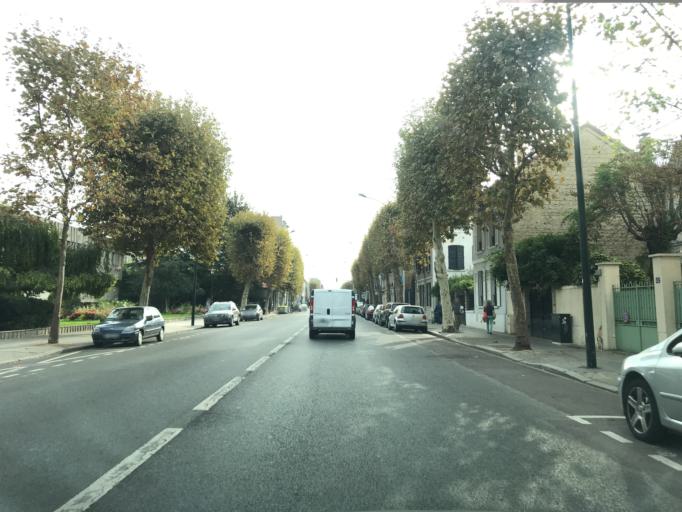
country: FR
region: Ile-de-France
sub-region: Departement des Hauts-de-Seine
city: La Garenne-Colombes
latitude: 48.9067
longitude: 2.2459
